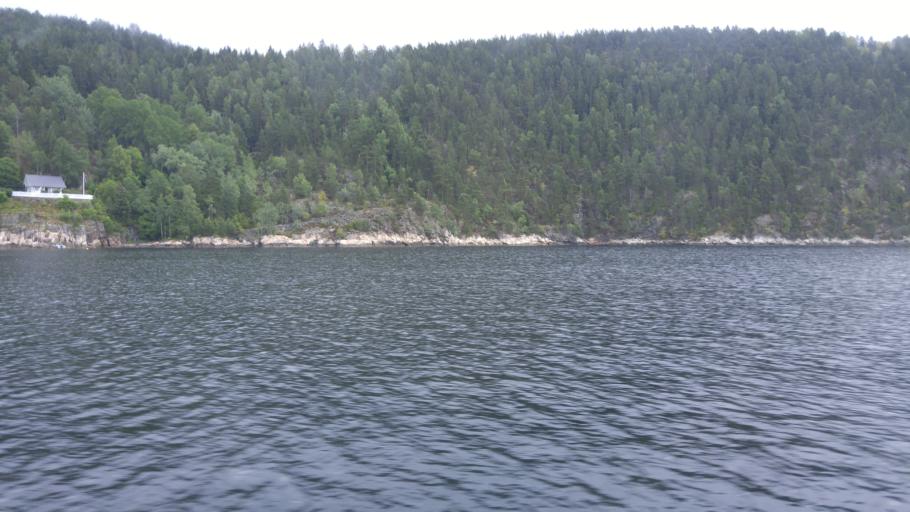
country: NO
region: Akershus
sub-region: Nesodden
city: Nesoddtangen
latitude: 59.8125
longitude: 10.6120
